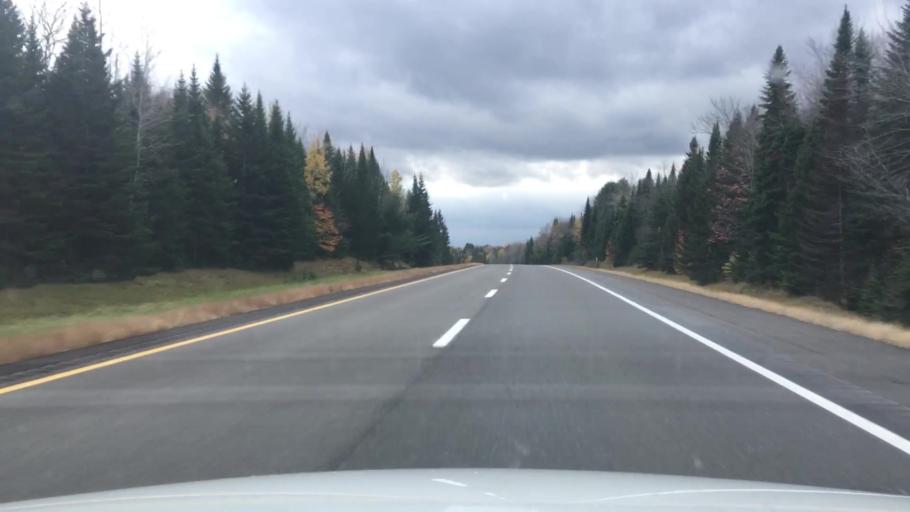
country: US
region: Maine
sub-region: Penobscot County
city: Patten
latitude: 46.0901
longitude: -68.2031
